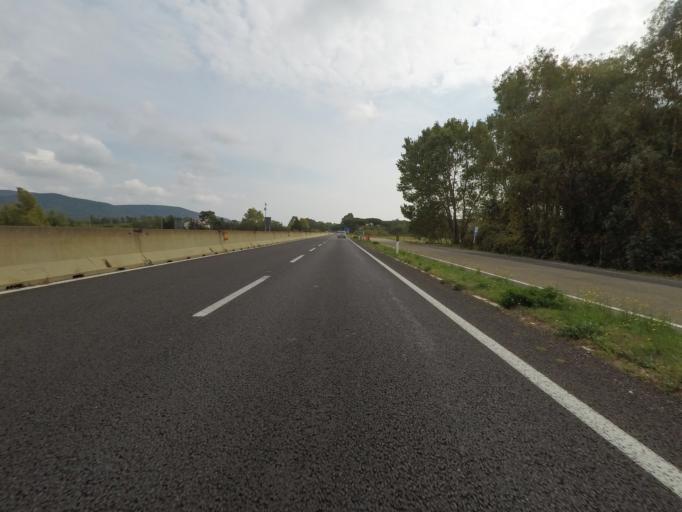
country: IT
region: Tuscany
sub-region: Provincia di Grosseto
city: Albinia
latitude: 42.4838
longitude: 11.2188
